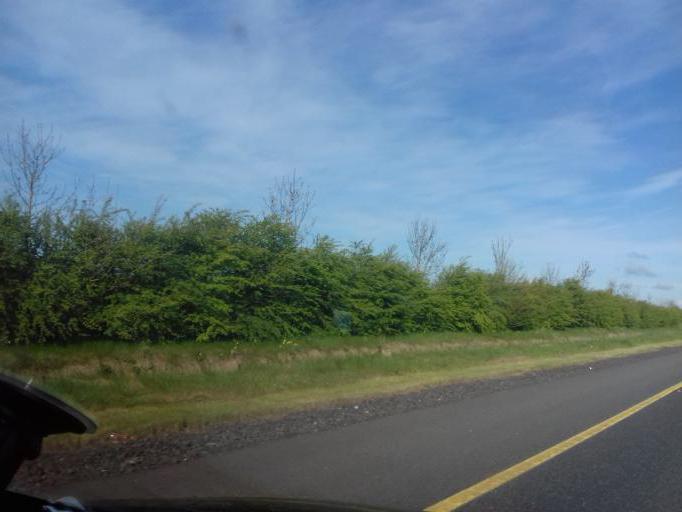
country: IE
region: Leinster
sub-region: An Mhi
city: Kells
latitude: 53.6848
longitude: -6.8026
